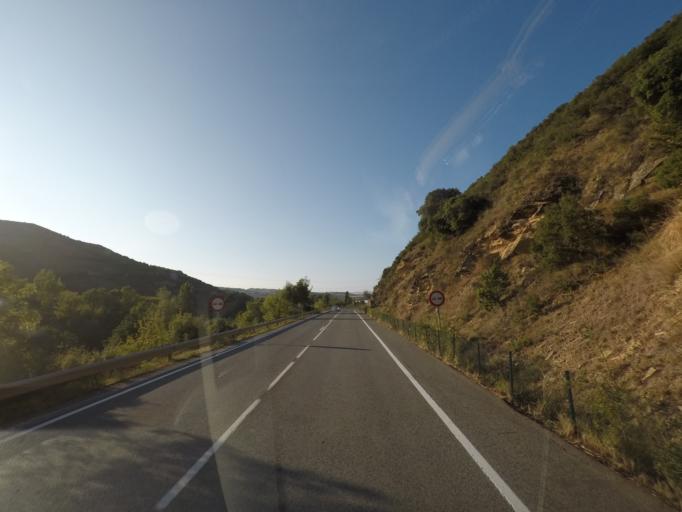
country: ES
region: Navarre
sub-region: Provincia de Navarra
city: Liedena
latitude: 42.6029
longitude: -1.2768
